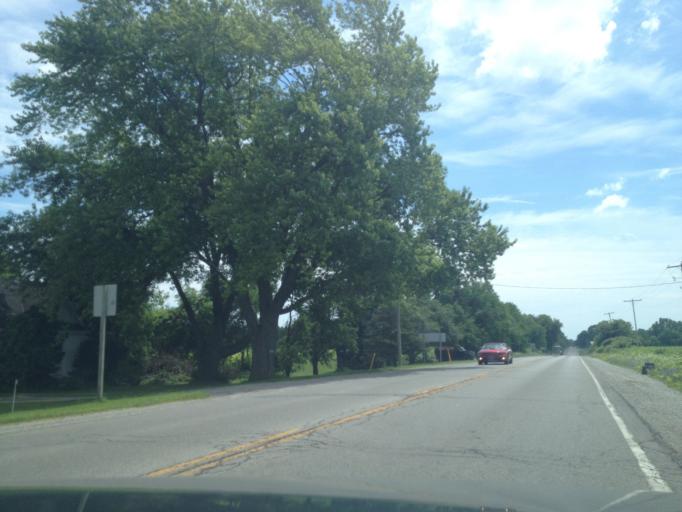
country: CA
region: Ontario
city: Norfolk County
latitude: 42.7828
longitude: -80.2841
